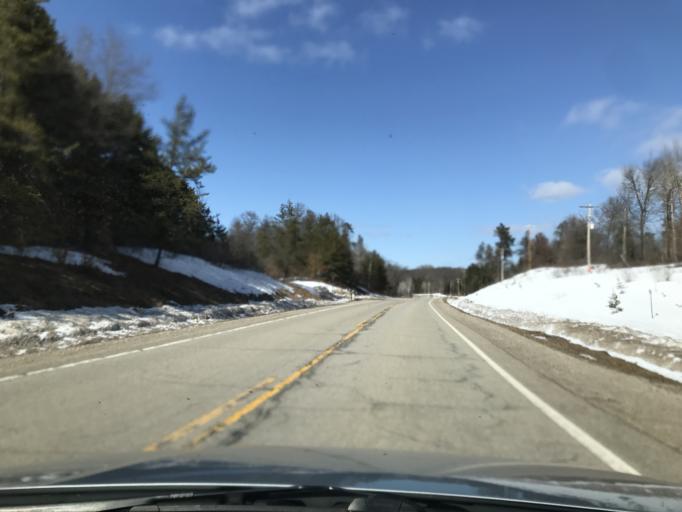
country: US
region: Wisconsin
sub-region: Marinette County
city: Peshtigo
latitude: 45.3332
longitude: -88.1016
